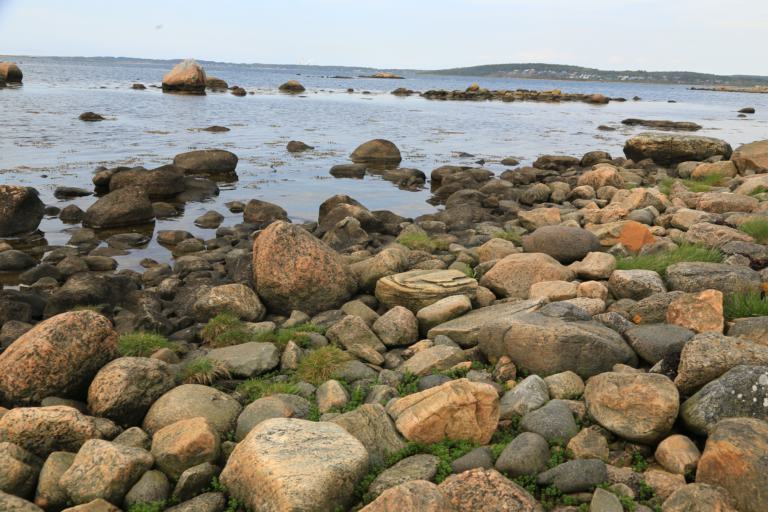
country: SE
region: Halland
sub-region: Varbergs Kommun
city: Varberg
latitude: 57.1500
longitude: 12.2069
